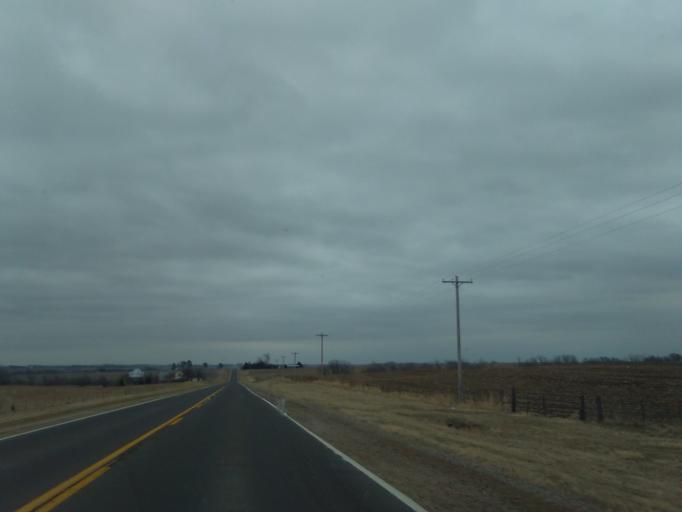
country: US
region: Nebraska
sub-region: Richardson County
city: Falls City
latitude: 40.0583
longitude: -95.5725
